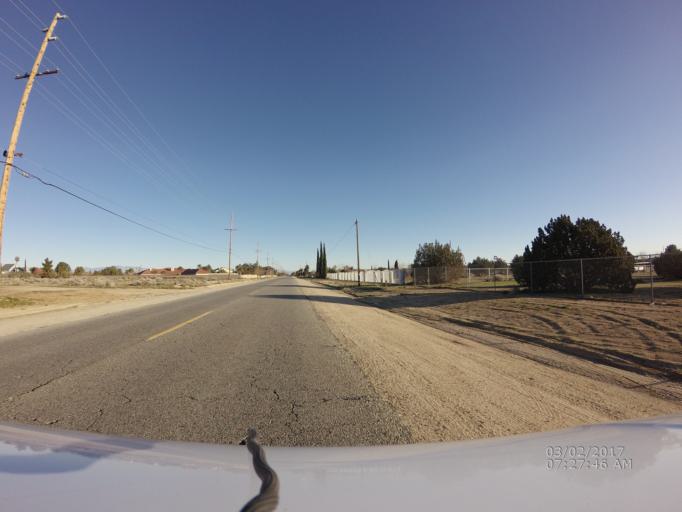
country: US
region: California
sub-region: Los Angeles County
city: Desert View Highlands
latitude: 34.6070
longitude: -118.1654
